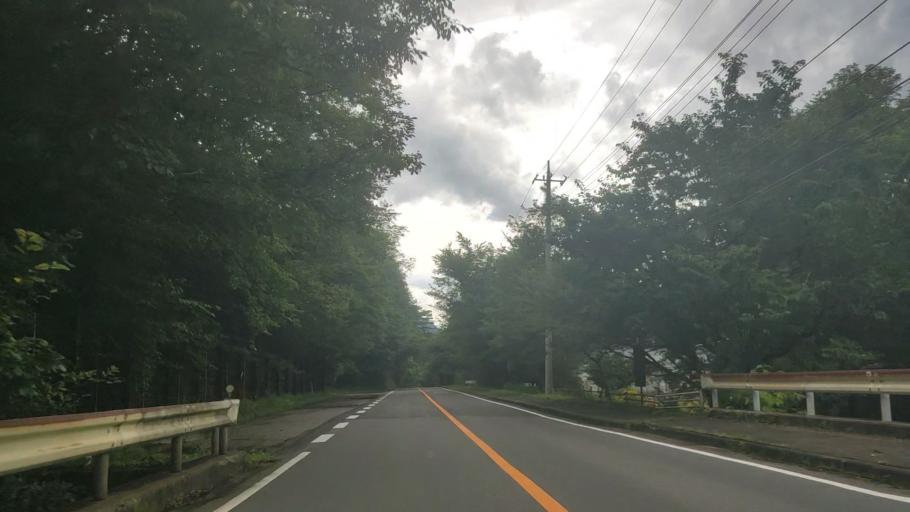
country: JP
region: Tochigi
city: Nikko
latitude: 36.6272
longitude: 139.4331
